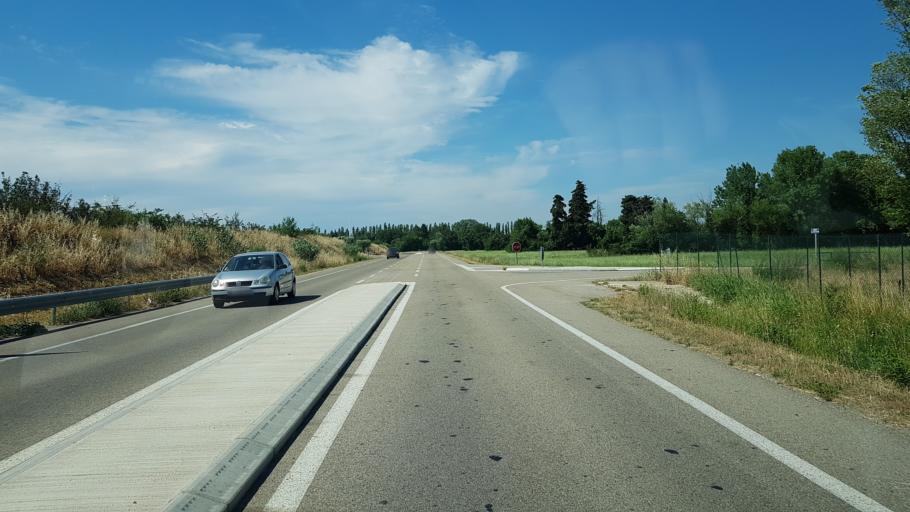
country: FR
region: Provence-Alpes-Cote d'Azur
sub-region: Departement des Bouches-du-Rhone
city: Saint-Martin-de-Crau
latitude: 43.6390
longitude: 4.8288
